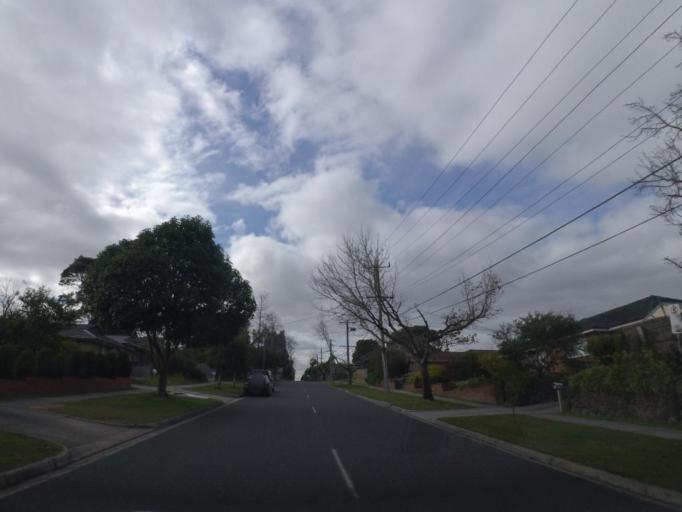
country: AU
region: Victoria
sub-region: Maroondah
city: Ringwood East
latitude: -37.7992
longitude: 145.2418
